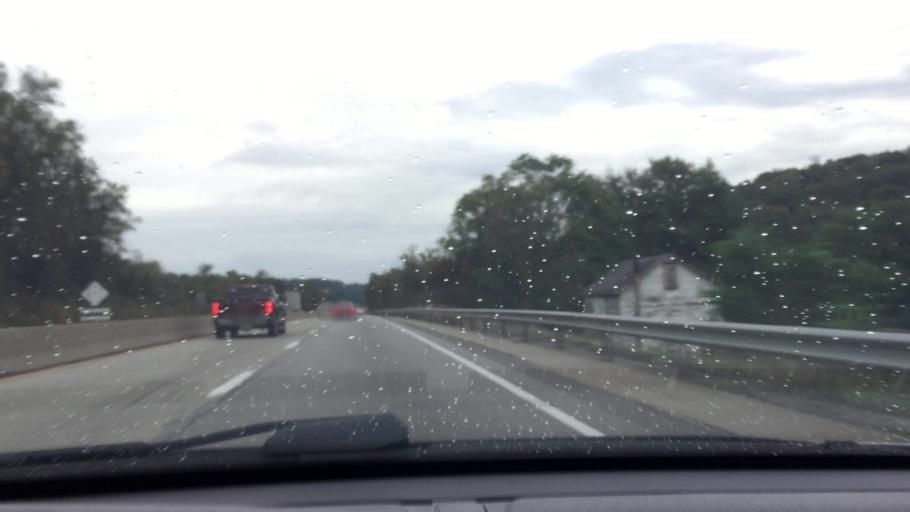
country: US
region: Pennsylvania
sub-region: Washington County
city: Speers
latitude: 40.1121
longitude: -79.8919
